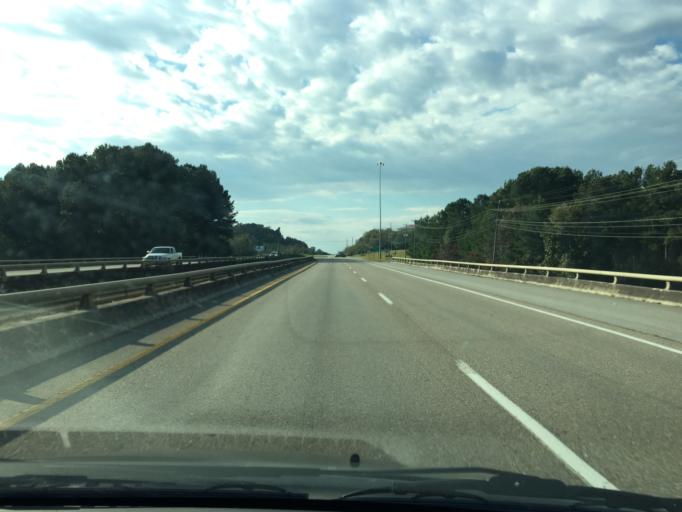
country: US
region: Tennessee
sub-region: Loudon County
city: Loudon
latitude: 35.7327
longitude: -84.3942
